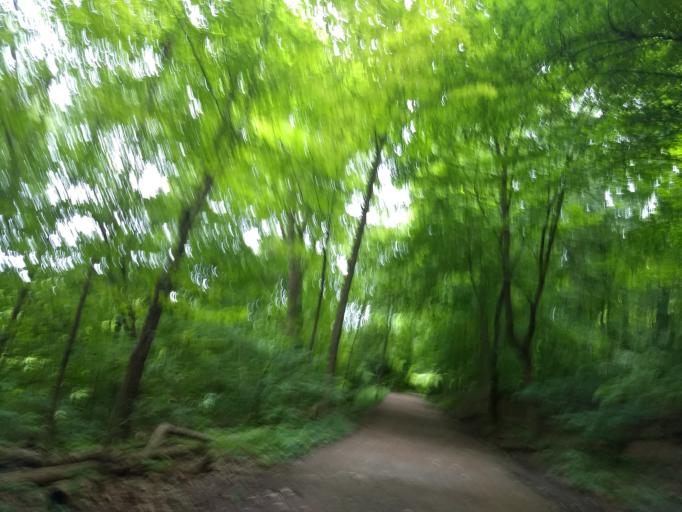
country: US
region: Pennsylvania
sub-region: Allegheny County
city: Wilkinsburg
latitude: 40.4386
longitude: -79.9010
